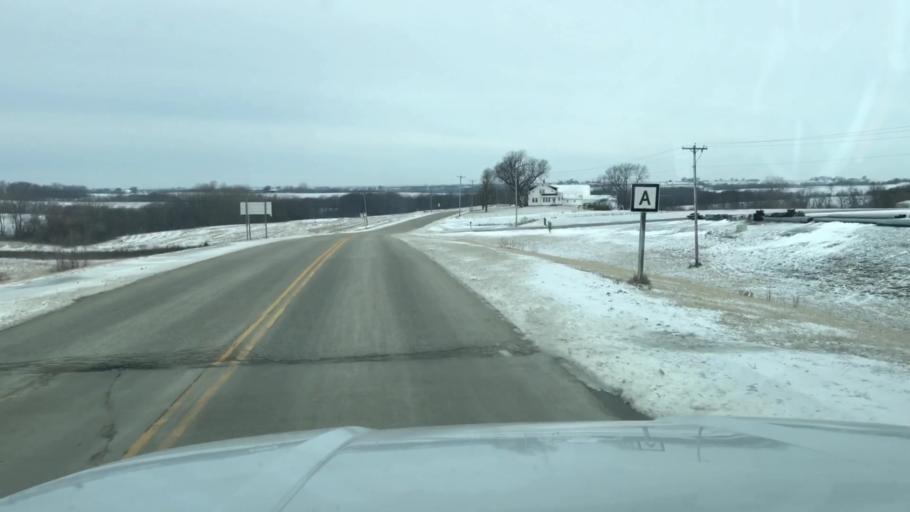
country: US
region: Missouri
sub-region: Andrew County
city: Savannah
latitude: 40.0254
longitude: -94.8805
